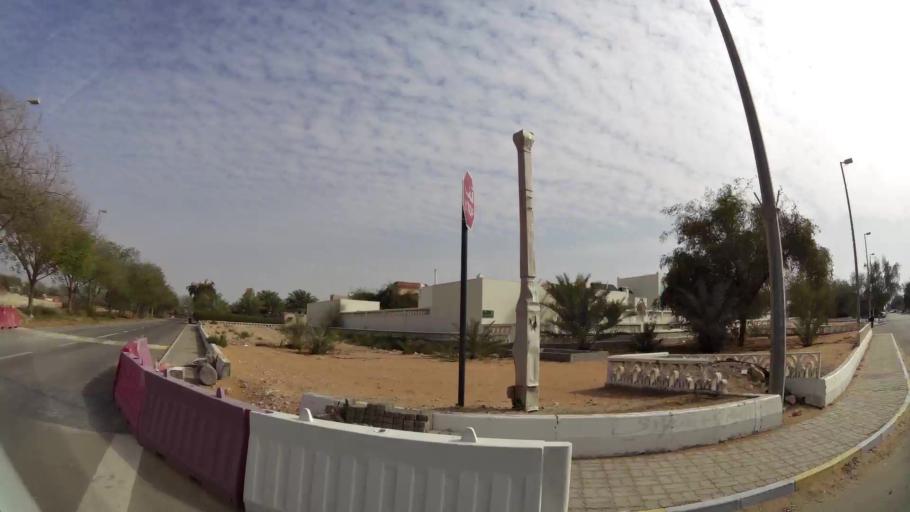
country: AE
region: Abu Dhabi
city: Abu Dhabi
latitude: 24.6061
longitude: 54.7016
